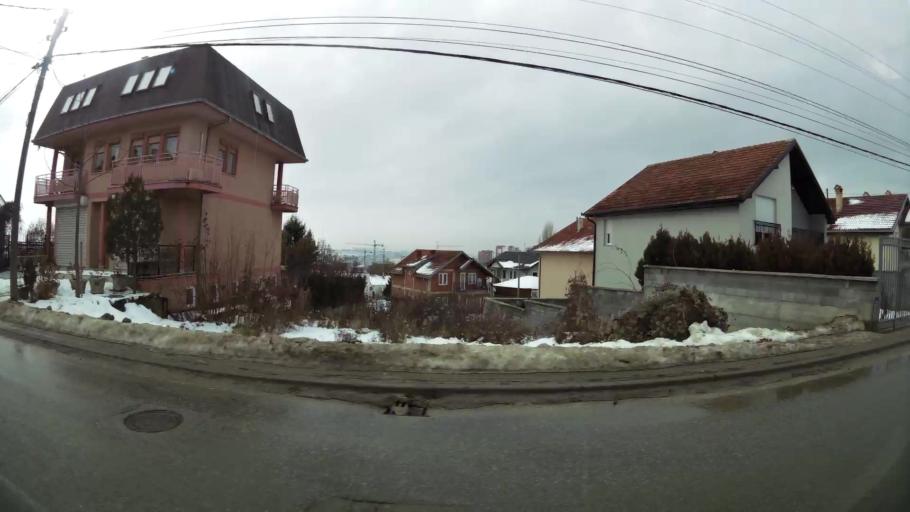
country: XK
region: Pristina
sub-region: Komuna e Prishtines
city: Pristina
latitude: 42.6510
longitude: 21.1936
